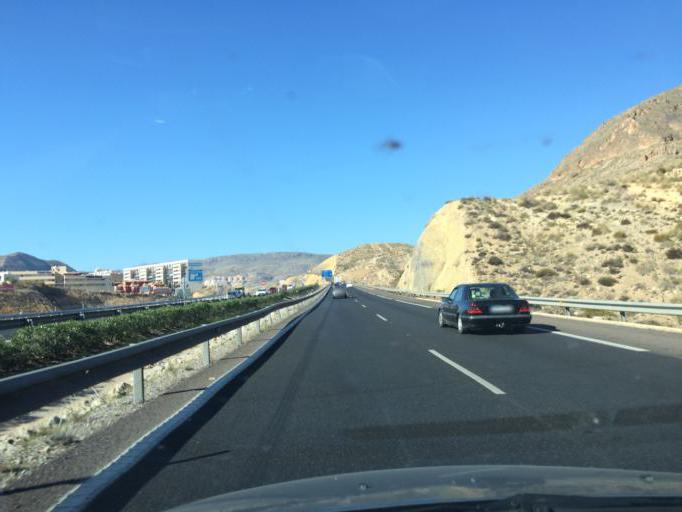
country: ES
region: Andalusia
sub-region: Provincia de Almeria
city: Aguadulce
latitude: 36.8251
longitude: -2.5796
